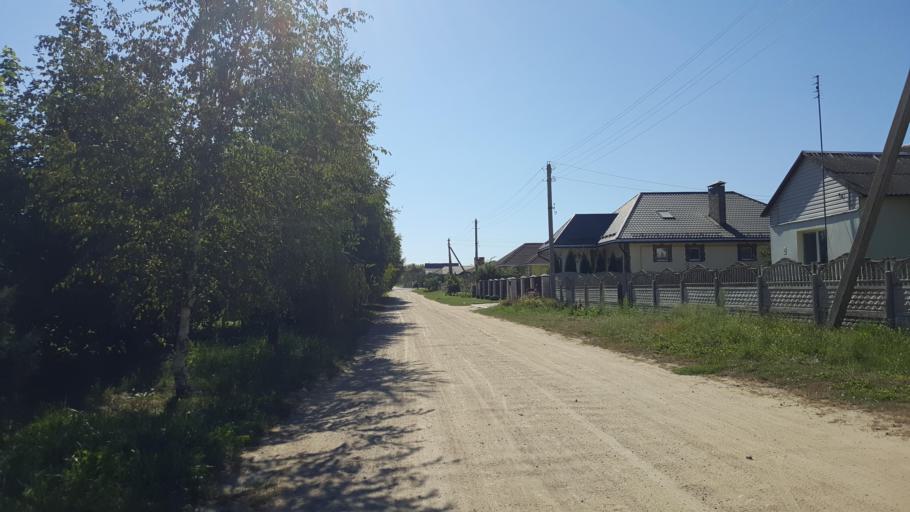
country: BY
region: Brest
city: Vysokaye
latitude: 52.2615
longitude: 23.5031
